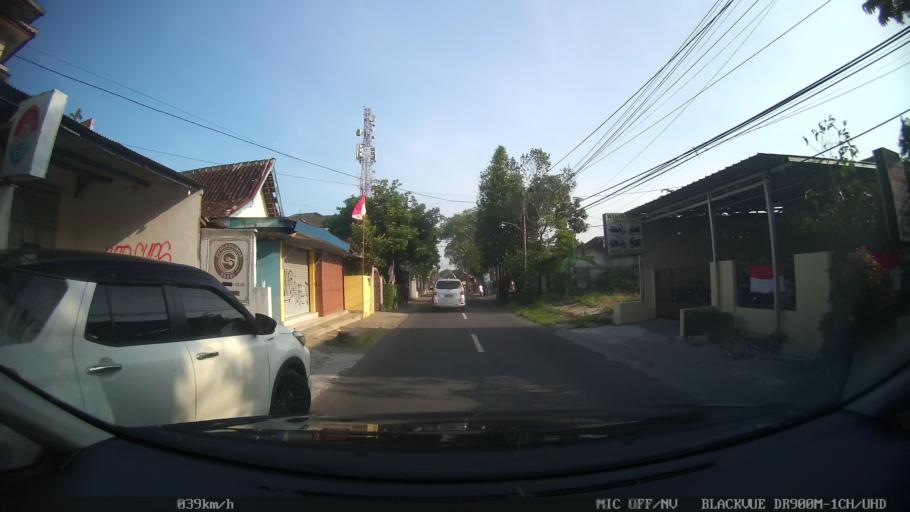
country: ID
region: Daerah Istimewa Yogyakarta
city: Depok
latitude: -7.7751
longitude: 110.4047
